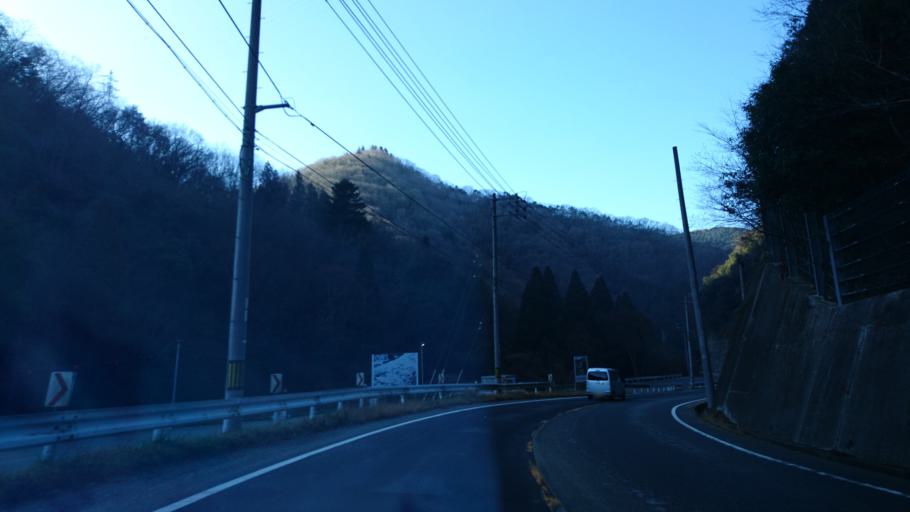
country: JP
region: Okayama
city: Takahashi
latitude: 34.8203
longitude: 133.6537
